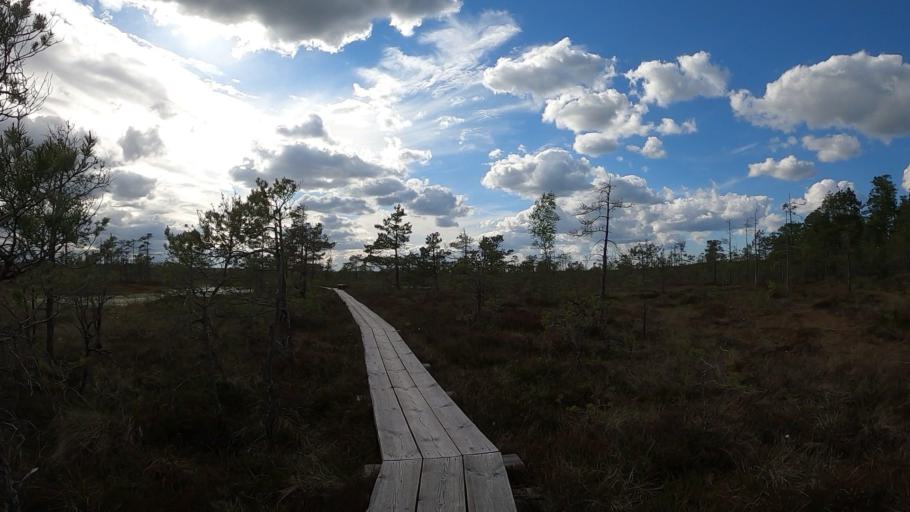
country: LV
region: Babite
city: Pinki
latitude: 56.8538
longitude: 23.8233
